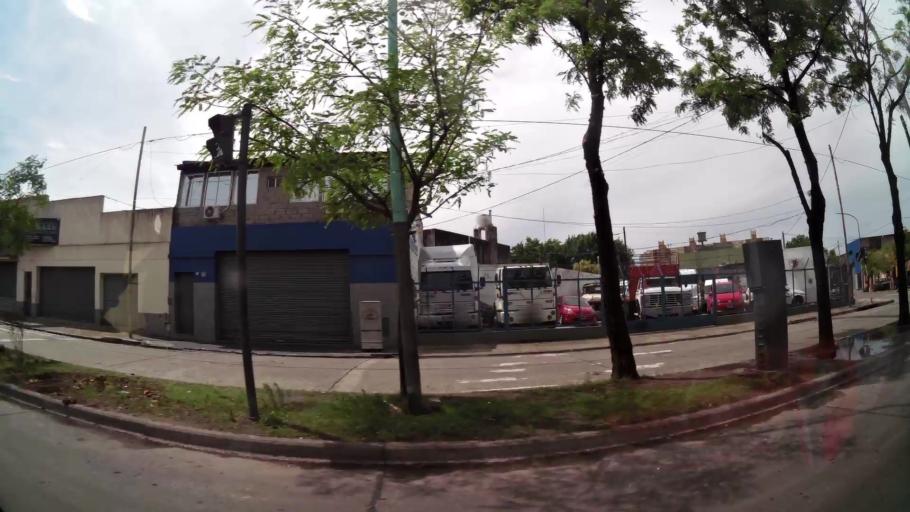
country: AR
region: Buenos Aires F.D.
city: Villa Lugano
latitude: -34.6503
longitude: -58.4595
